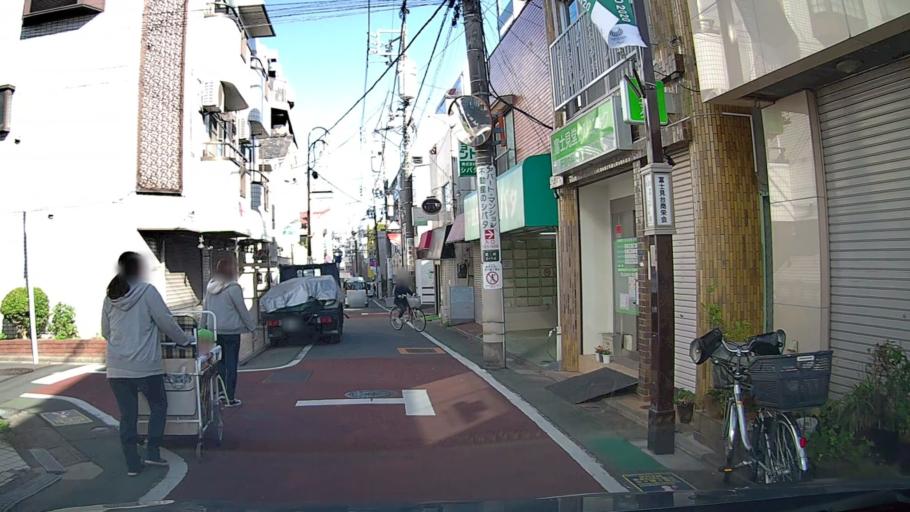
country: JP
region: Saitama
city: Wako
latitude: 35.7364
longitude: 139.6288
